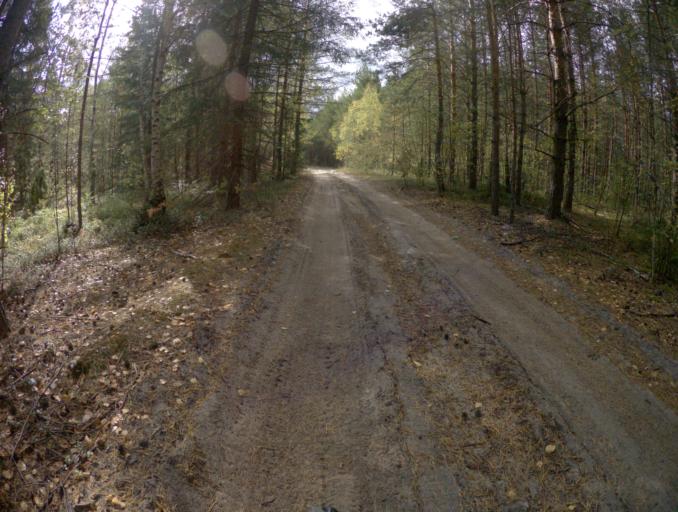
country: RU
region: Vladimir
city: Urshel'skiy
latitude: 55.8137
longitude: 40.1663
